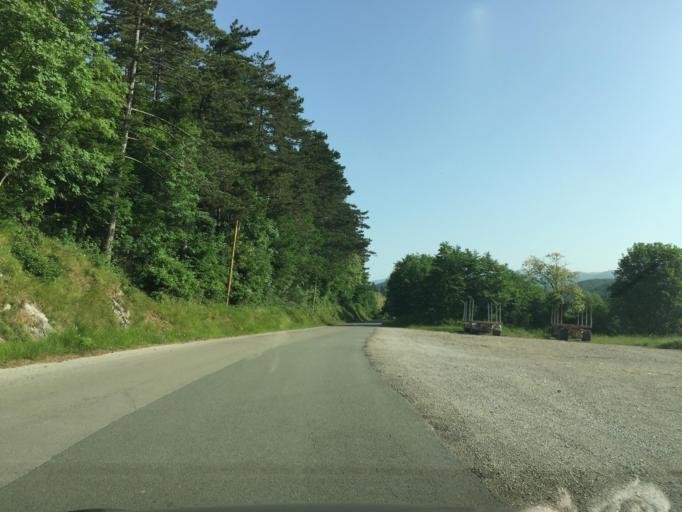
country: HR
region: Primorsko-Goranska
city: Klana
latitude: 45.4569
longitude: 14.3779
